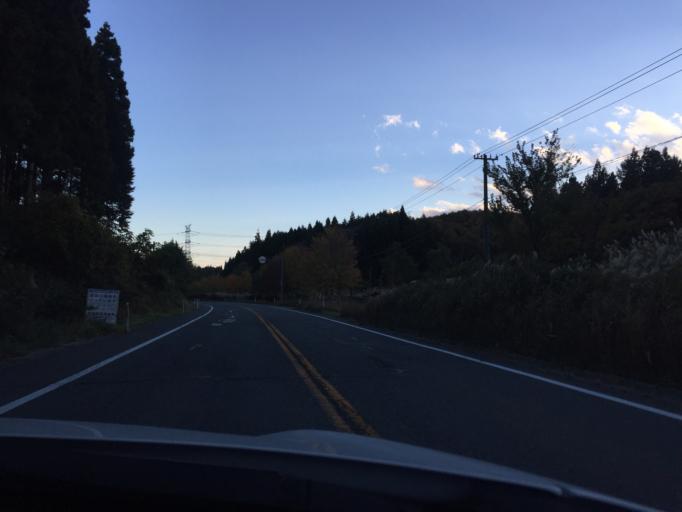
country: JP
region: Fukushima
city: Ishikawa
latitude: 37.2034
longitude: 140.6106
